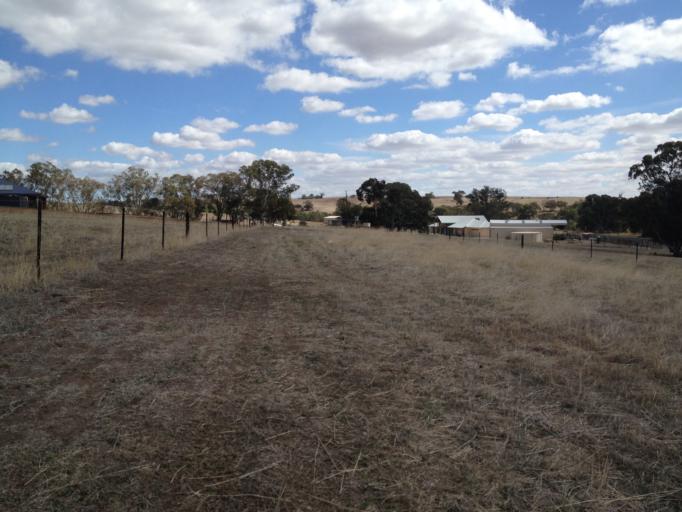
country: AU
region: South Australia
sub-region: Barossa
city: Lyndoch
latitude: -34.6290
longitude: 138.8357
